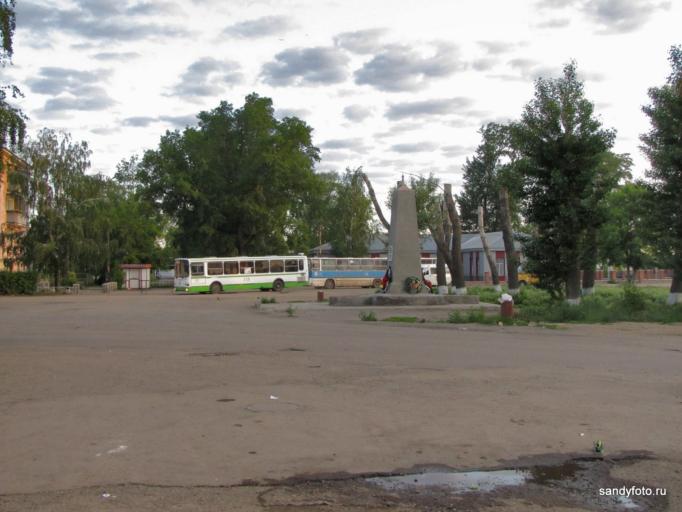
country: RU
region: Chelyabinsk
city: Troitsk
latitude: 54.1126
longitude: 61.5690
